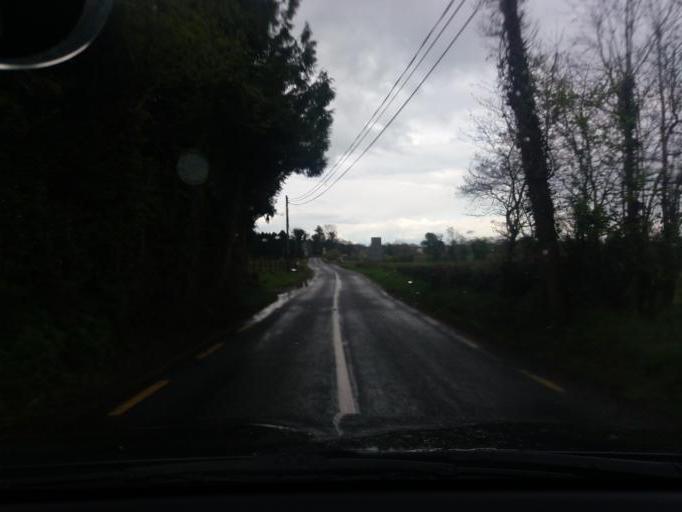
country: IE
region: Ulster
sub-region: An Cabhan
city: Ballyconnell
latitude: 54.1295
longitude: -7.6867
